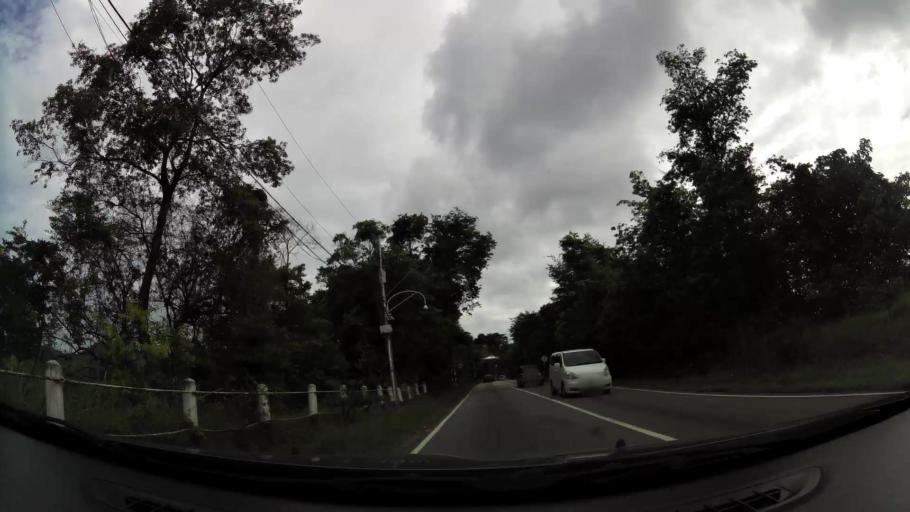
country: TT
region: City of Port of Spain
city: Port-of-Spain
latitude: 10.6740
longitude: -61.5043
